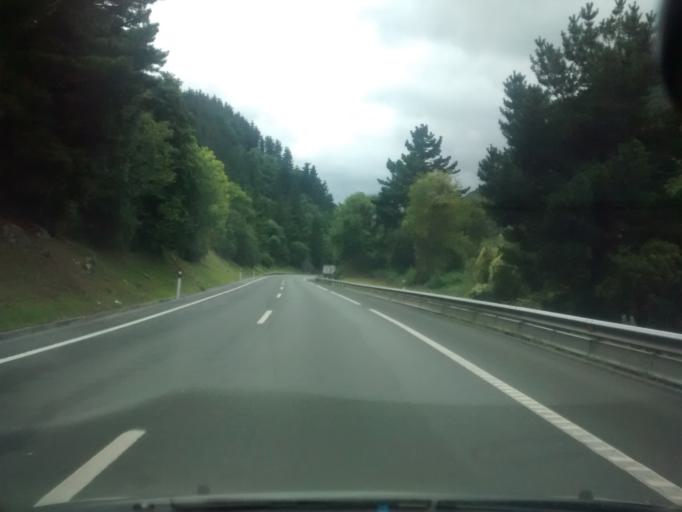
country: ES
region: Basque Country
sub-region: Provincia de Guipuzcoa
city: Mendaro
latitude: 43.2728
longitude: -2.3680
